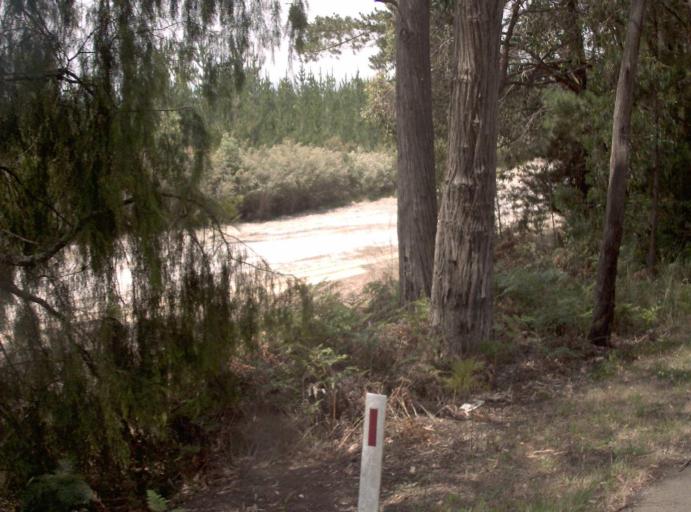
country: AU
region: Victoria
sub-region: Latrobe
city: Traralgon
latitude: -38.2743
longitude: 146.6923
